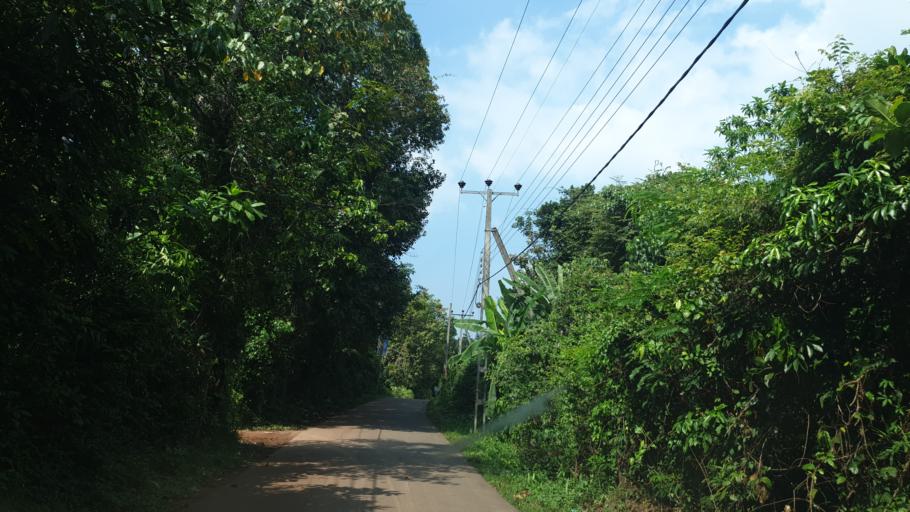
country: LK
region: Western
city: Panadura
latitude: 6.7329
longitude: 79.9528
